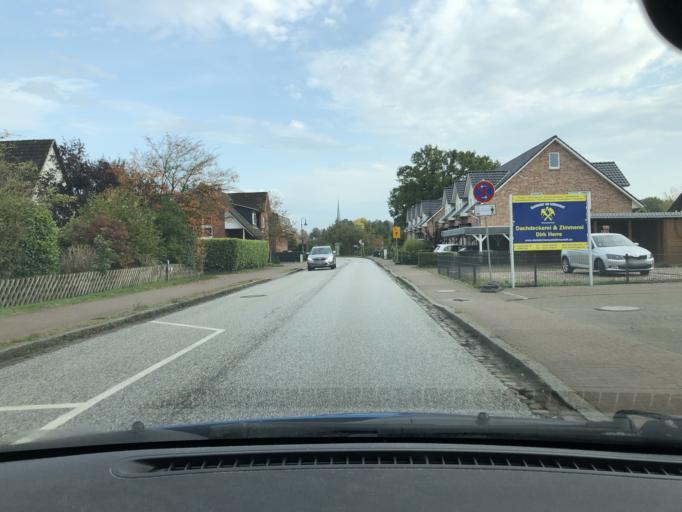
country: DE
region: Schleswig-Holstein
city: Siek
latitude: 53.6375
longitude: 10.2897
